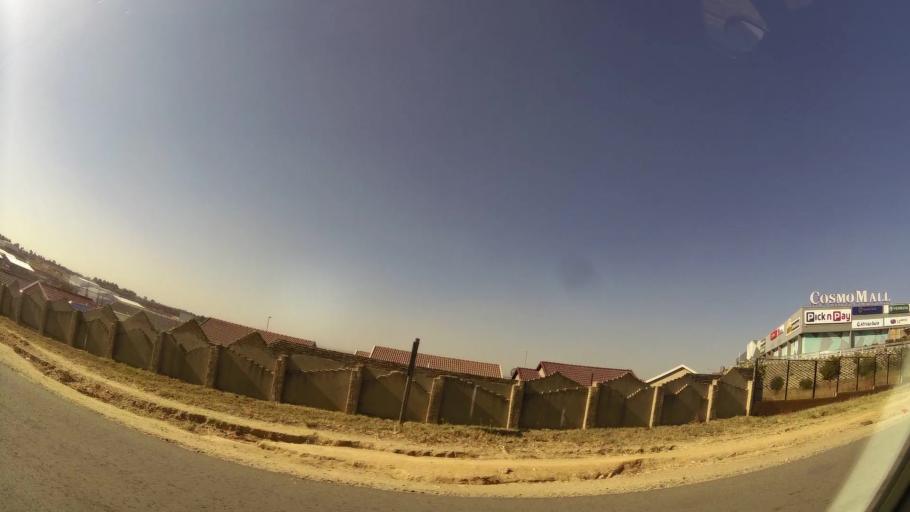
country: ZA
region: Gauteng
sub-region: West Rand District Municipality
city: Muldersdriseloop
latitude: -26.0125
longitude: 27.9379
